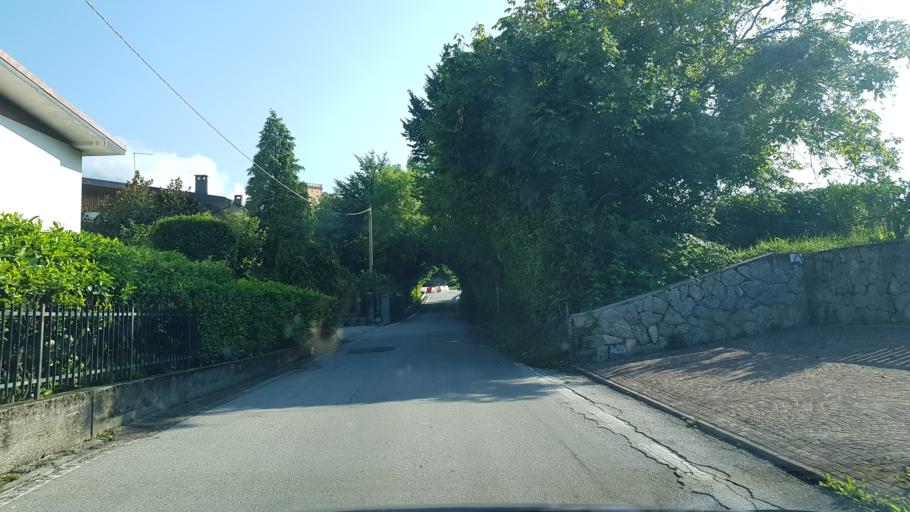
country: IT
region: Veneto
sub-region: Provincia di Belluno
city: Castion
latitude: 46.1263
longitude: 12.2167
